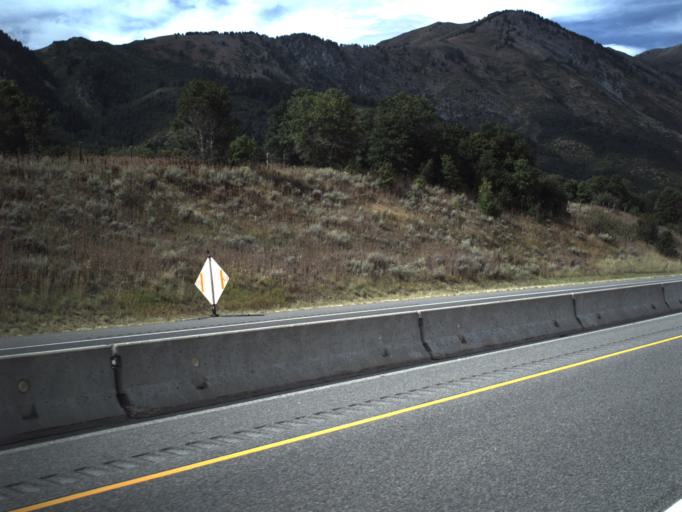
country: US
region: Utah
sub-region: Cache County
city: Wellsville
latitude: 41.5875
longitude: -111.9761
